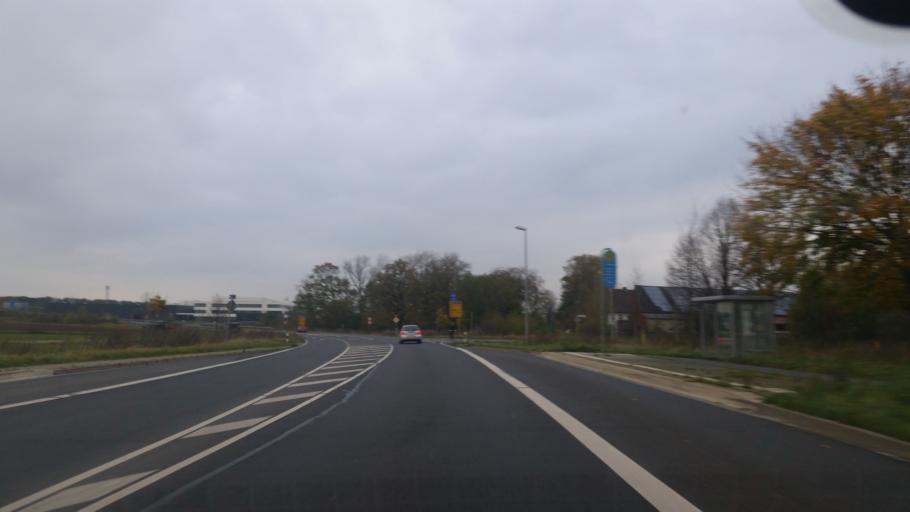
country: DE
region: Lower Saxony
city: Leiferde
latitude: 52.2051
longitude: 10.4956
